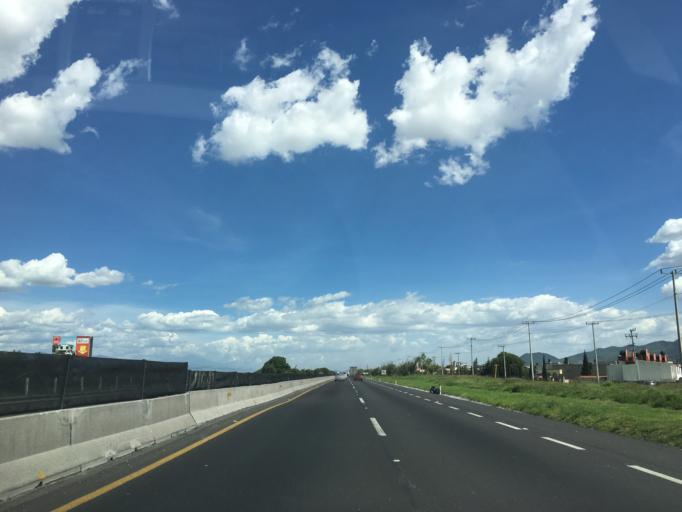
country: MX
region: Mexico
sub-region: Tonanitla
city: Colonia la Asuncion
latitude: 19.6846
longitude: -99.0756
